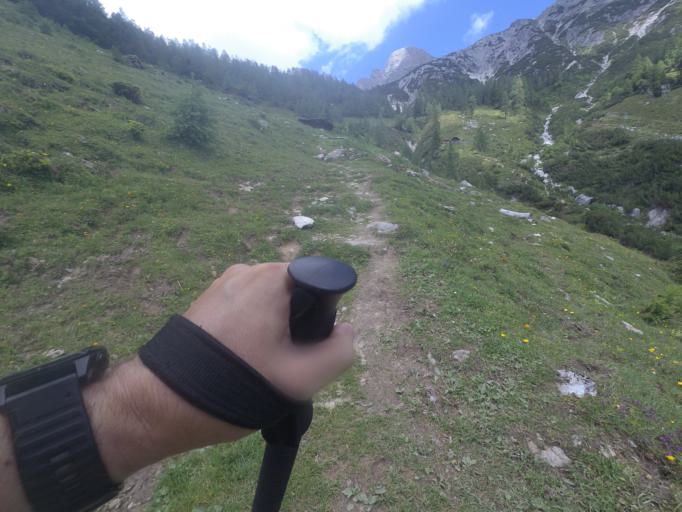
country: AT
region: Salzburg
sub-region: Politischer Bezirk Zell am See
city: Leogang
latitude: 47.4651
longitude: 12.7732
